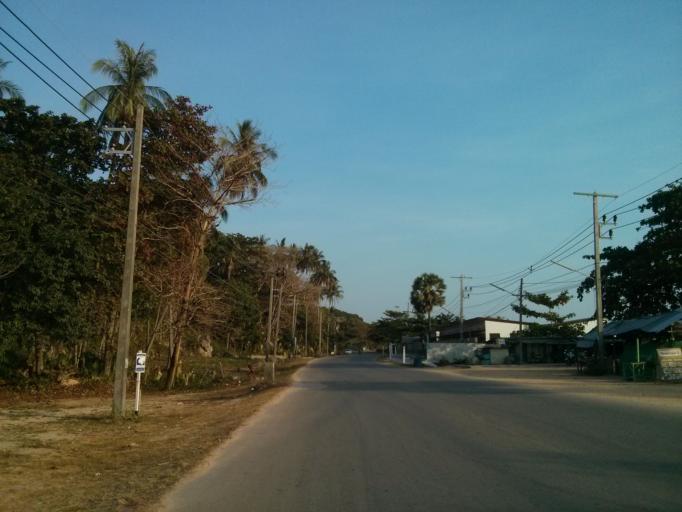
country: TH
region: Krabi
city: Ko Lanta
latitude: 7.5560
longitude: 99.0395
